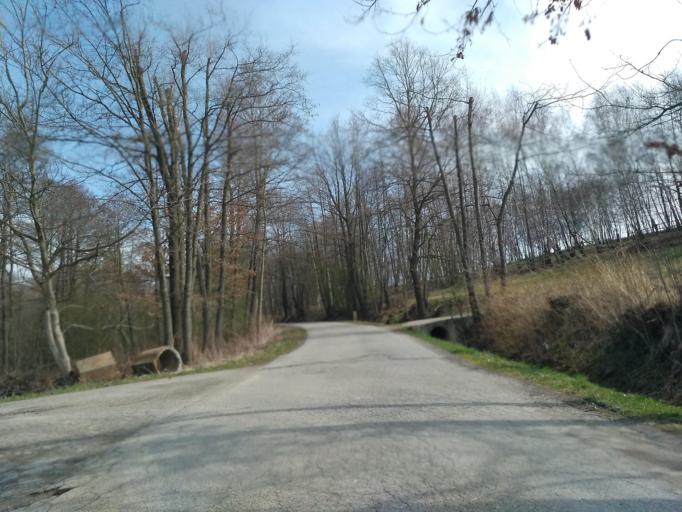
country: PL
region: Subcarpathian Voivodeship
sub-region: Powiat rzeszowski
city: Zglobien
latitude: 50.0261
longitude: 21.8099
